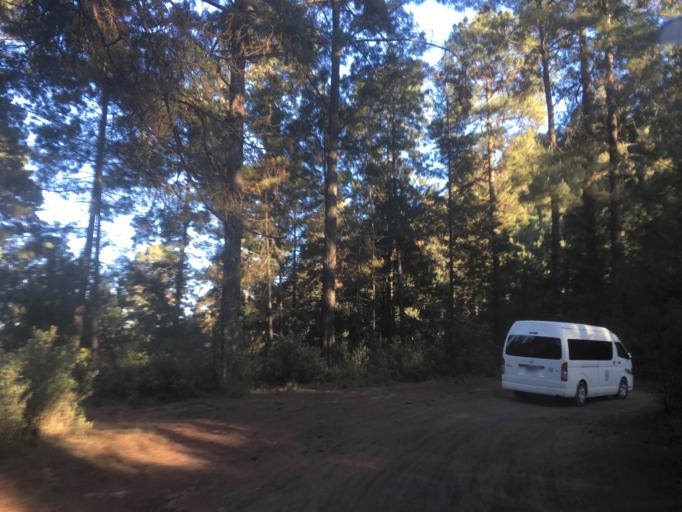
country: MX
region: Michoacan
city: Nuevo San Juan Parangaricutiro
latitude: 19.4585
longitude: -102.2055
